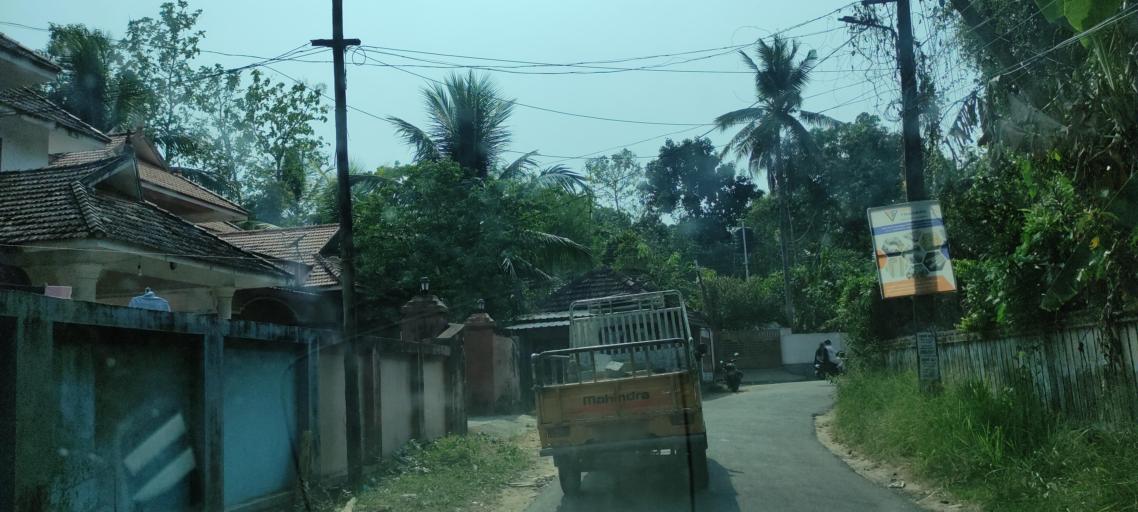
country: IN
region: Kerala
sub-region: Pattanamtitta
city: Tiruvalla
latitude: 9.3448
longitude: 76.5394
